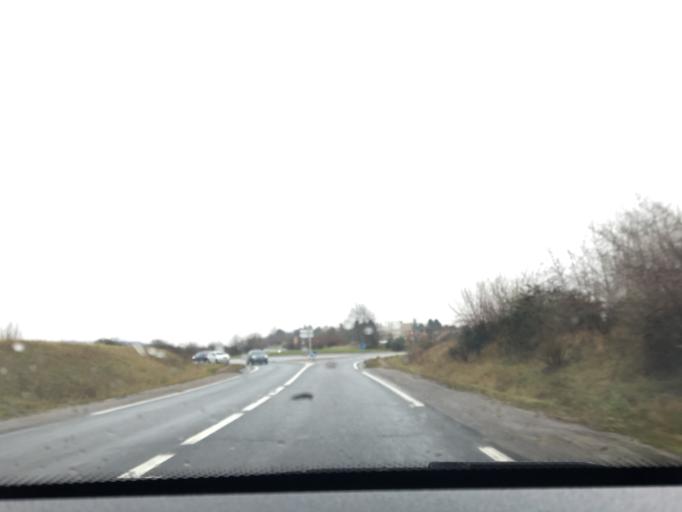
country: FR
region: Ile-de-France
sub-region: Departement des Yvelines
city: Limay
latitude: 49.0064
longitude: 1.7401
